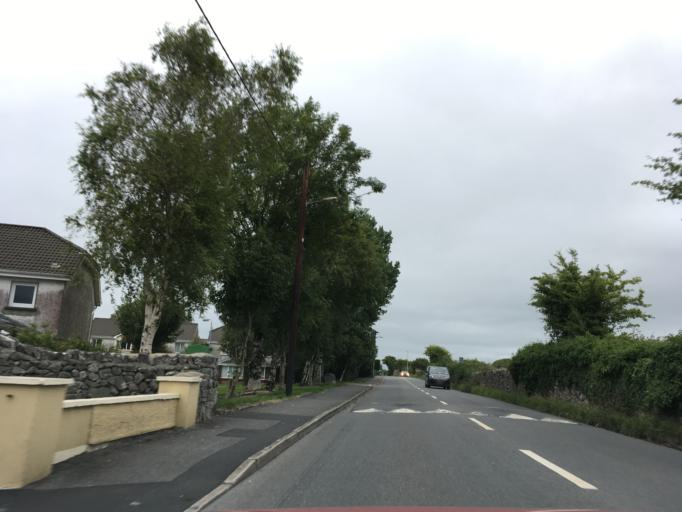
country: IE
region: Munster
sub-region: An Clar
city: Ennis
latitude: 52.8345
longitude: -8.9894
